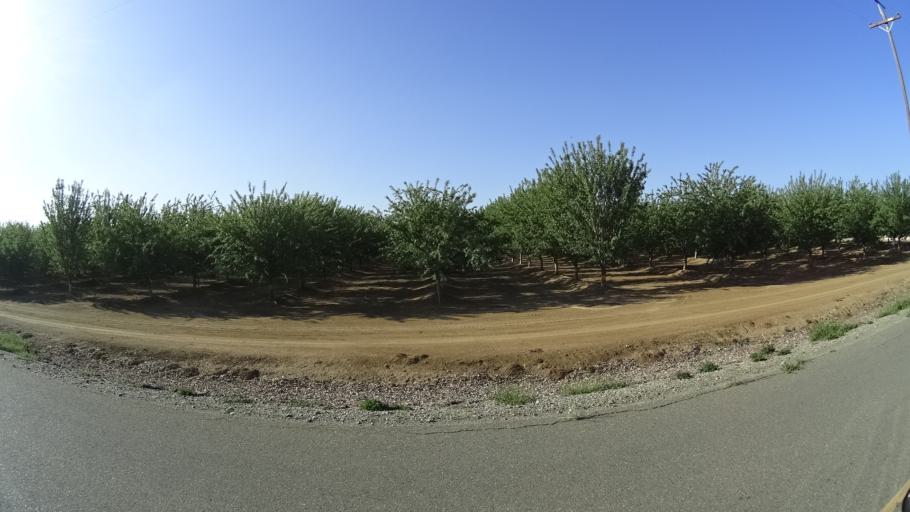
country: US
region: California
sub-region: Glenn County
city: Willows
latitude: 39.5096
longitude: -122.2321
